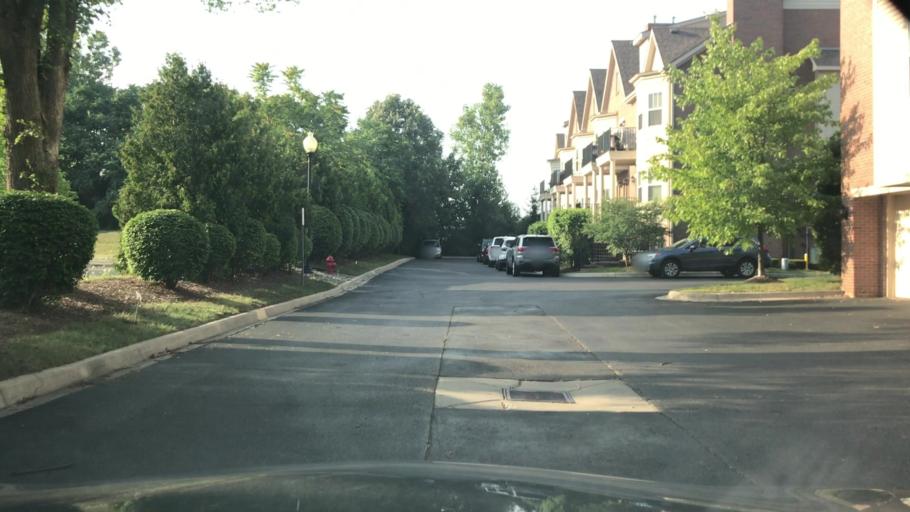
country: US
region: Michigan
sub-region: Oakland County
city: Novi
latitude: 42.4786
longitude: -83.4605
